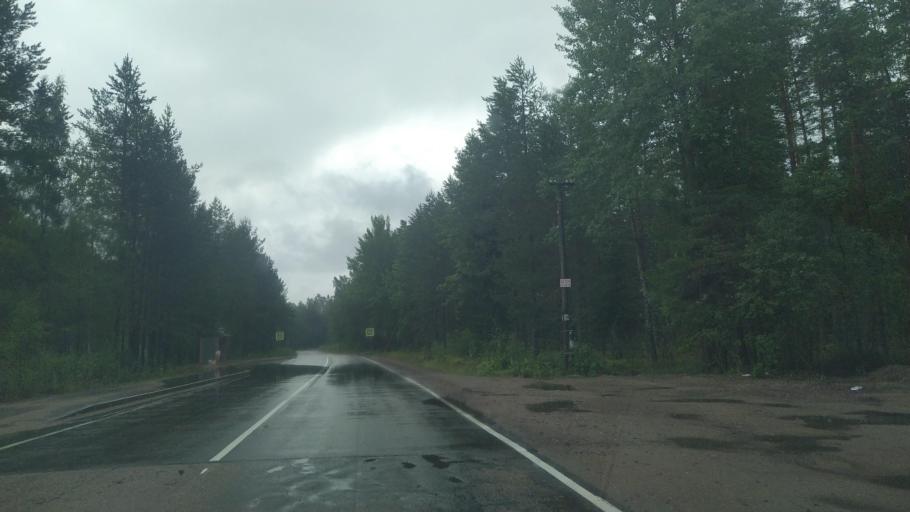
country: RU
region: Leningrad
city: Priozersk
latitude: 60.9765
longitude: 30.2783
